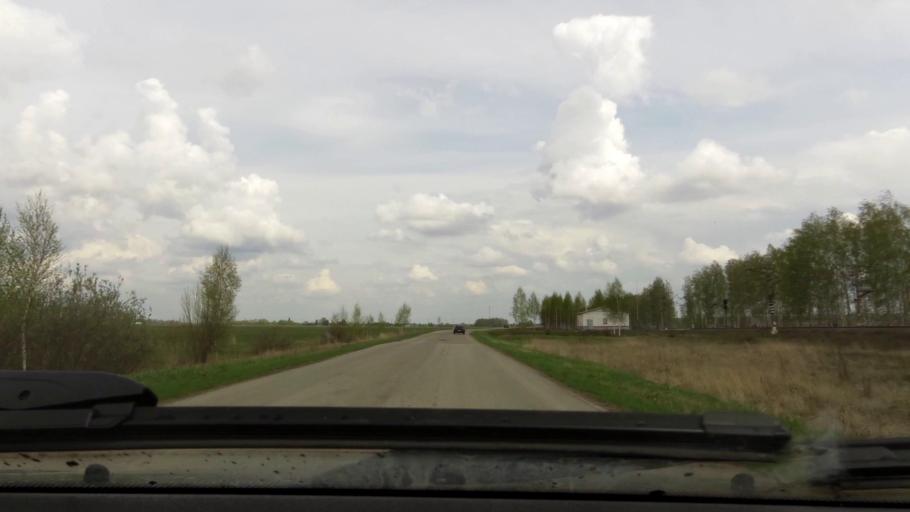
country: RU
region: Rjazan
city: Bagramovo
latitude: 54.7102
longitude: 39.3434
